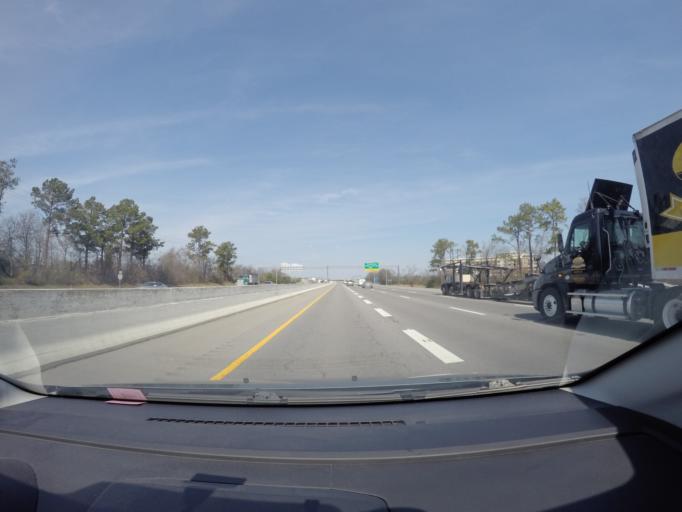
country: US
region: Tennessee
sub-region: Rutherford County
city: Murfreesboro
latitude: 35.8635
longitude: -86.4530
